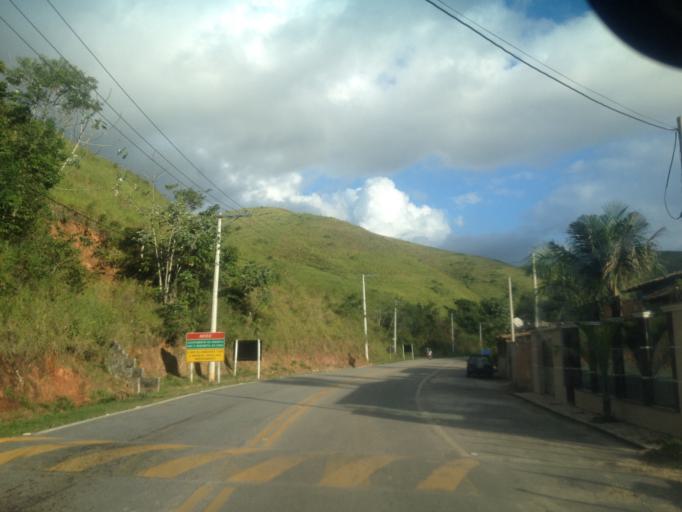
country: BR
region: Rio de Janeiro
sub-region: Quatis
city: Quatis
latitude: -22.2956
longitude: -44.2568
